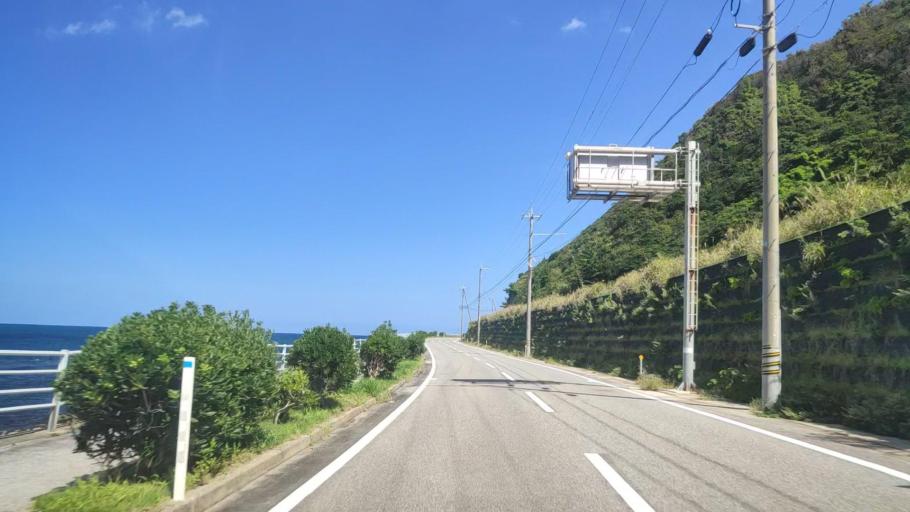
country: JP
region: Ishikawa
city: Nanao
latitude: 37.4782
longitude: 137.0998
